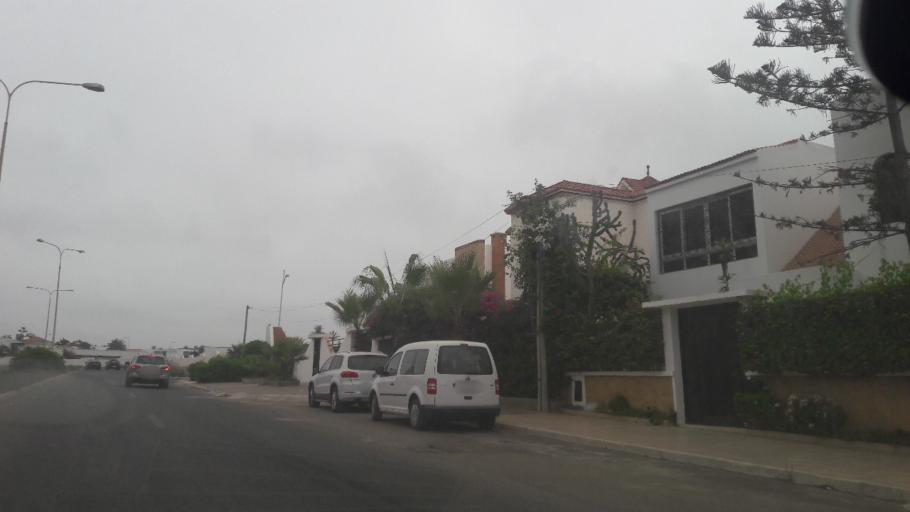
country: MA
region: Souss-Massa-Draa
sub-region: Agadir-Ida-ou-Tnan
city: Agadir
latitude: 30.3906
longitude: -9.5936
